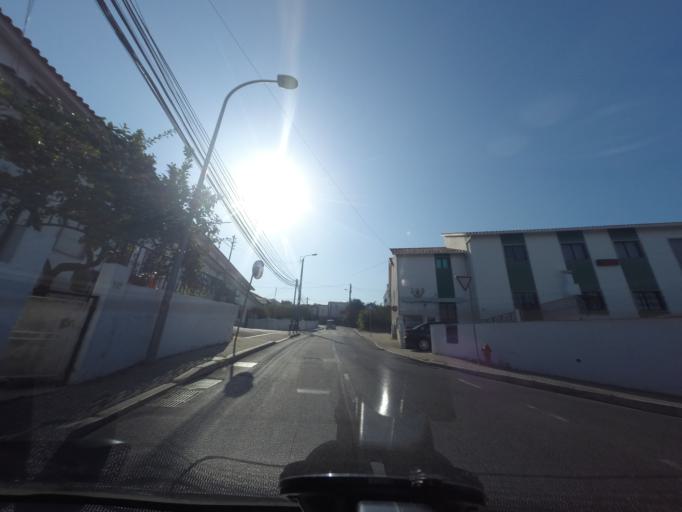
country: PT
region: Lisbon
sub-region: Cascais
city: Alcabideche
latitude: 38.7355
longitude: -9.3658
